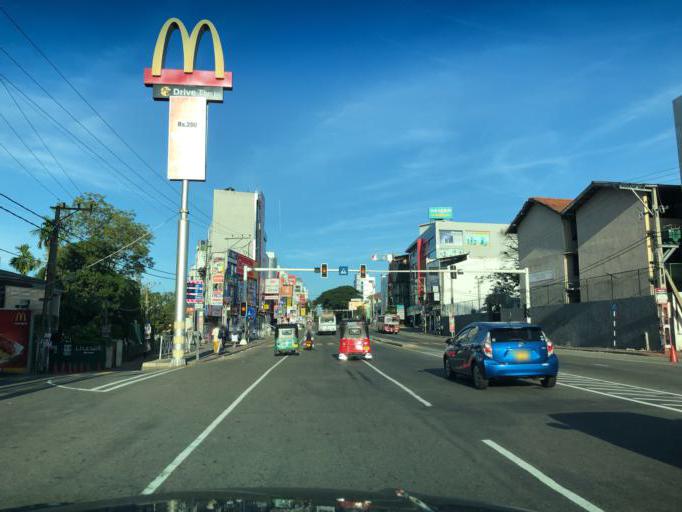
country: LK
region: Western
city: Sri Jayewardenepura Kotte
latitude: 6.8706
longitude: 79.8866
